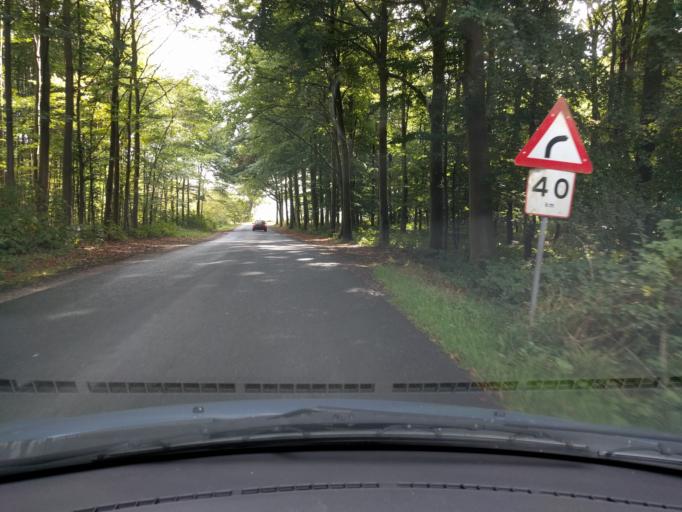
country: DK
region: South Denmark
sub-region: Kerteminde Kommune
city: Kerteminde
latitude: 55.4730
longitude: 10.6942
